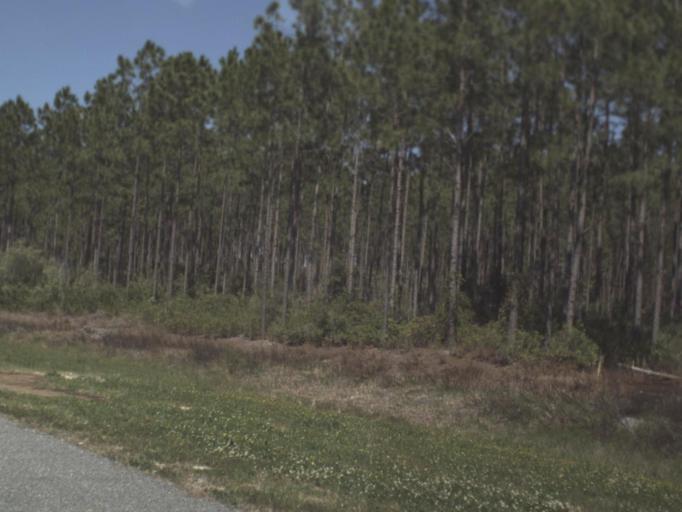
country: US
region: Florida
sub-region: Gulf County
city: Port Saint Joe
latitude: 29.8863
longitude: -85.3460
